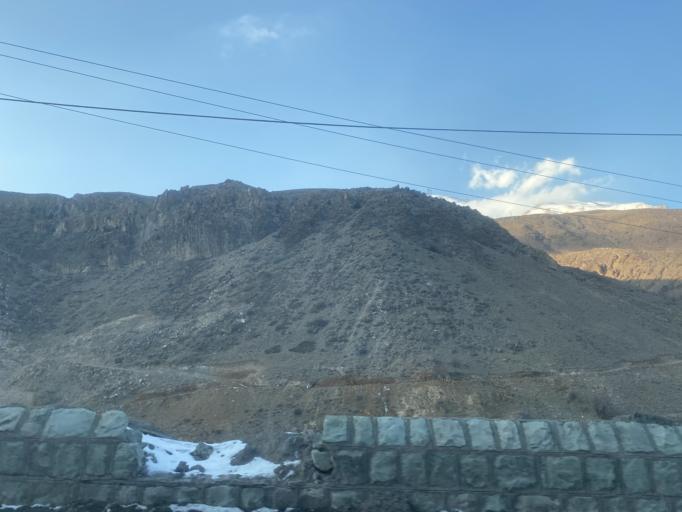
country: IR
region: Tehran
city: Damavand
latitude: 35.8618
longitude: 52.1352
